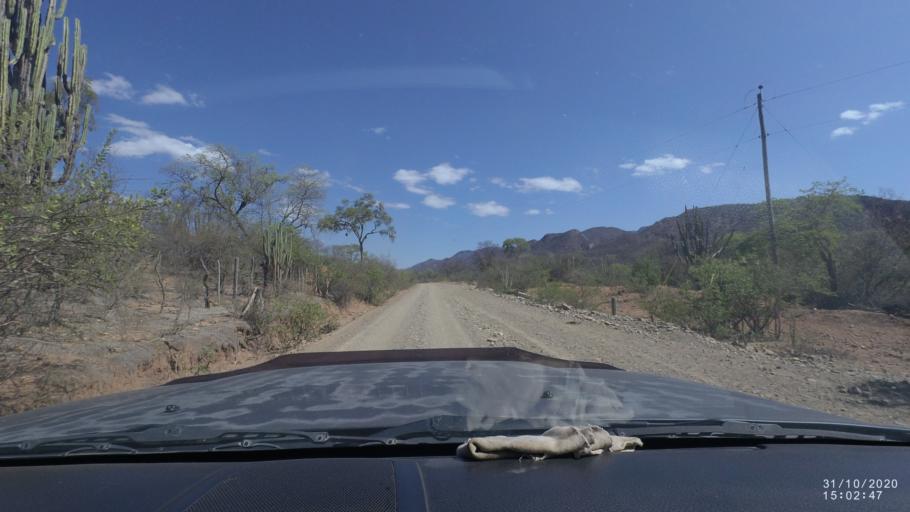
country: BO
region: Cochabamba
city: Aiquile
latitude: -18.2713
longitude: -64.8103
